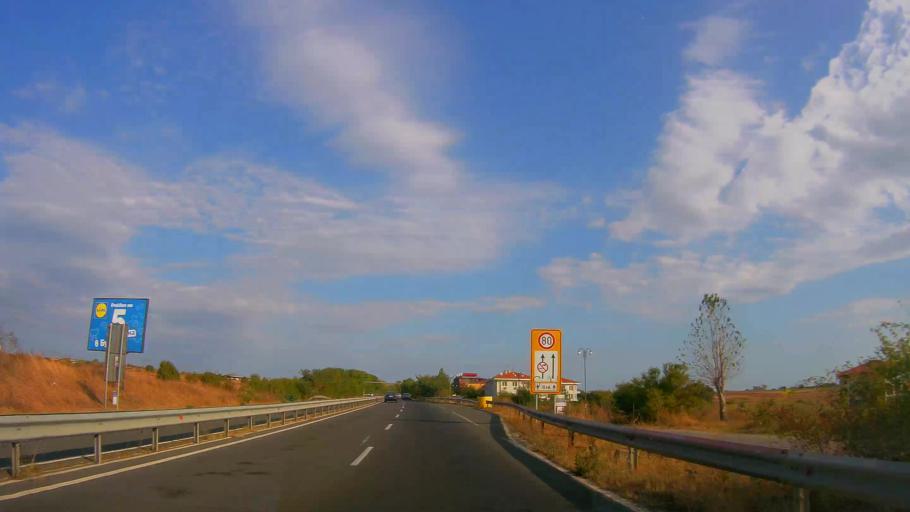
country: BG
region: Burgas
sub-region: Obshtina Sozopol
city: Chernomorets
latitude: 42.4301
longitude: 27.6395
